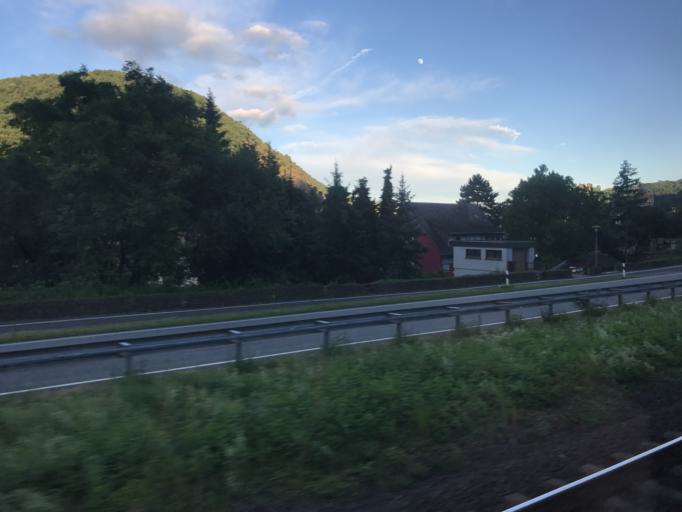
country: DE
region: Rheinland-Pfalz
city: Oberwesel
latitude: 50.1162
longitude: 7.7188
